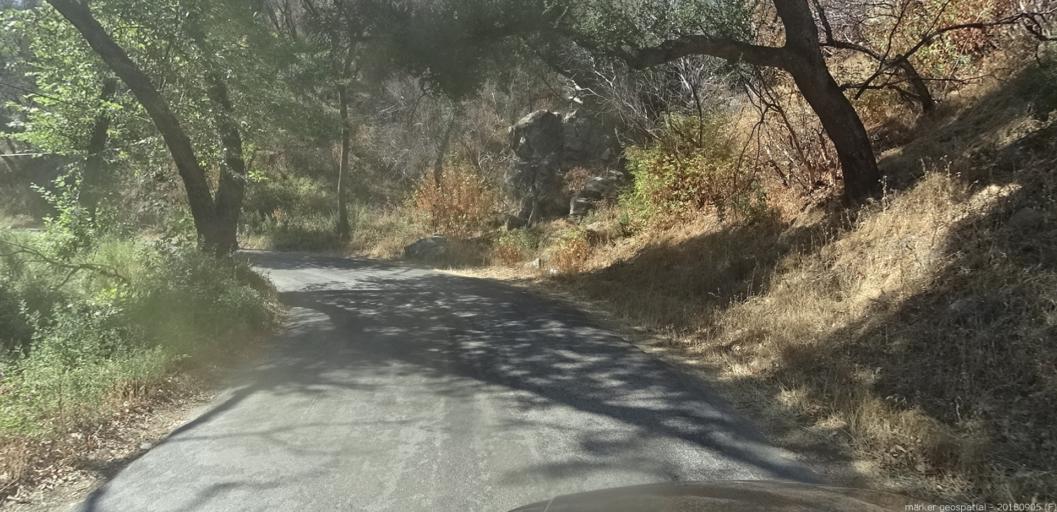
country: US
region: California
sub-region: Monterey County
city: Gonzales
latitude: 36.3849
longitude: -121.5954
